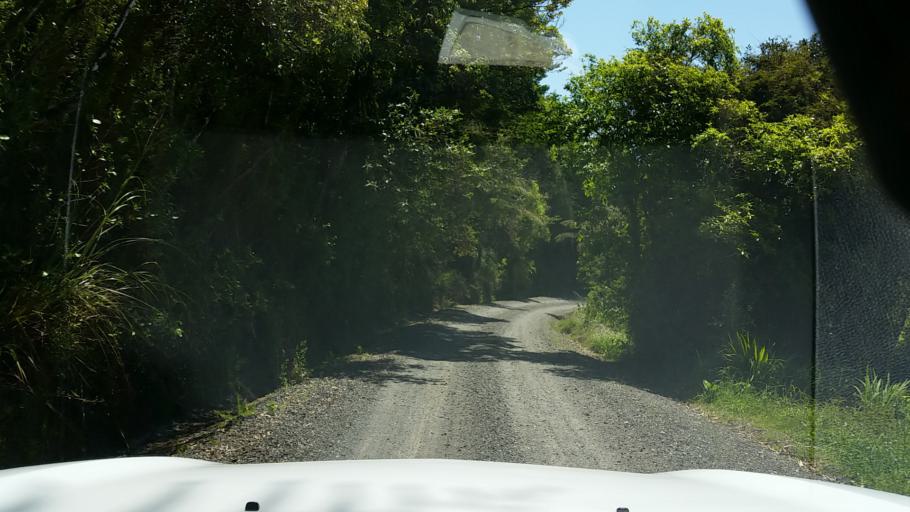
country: NZ
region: Auckland
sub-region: Auckland
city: Titirangi
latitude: -36.9276
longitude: 174.5821
